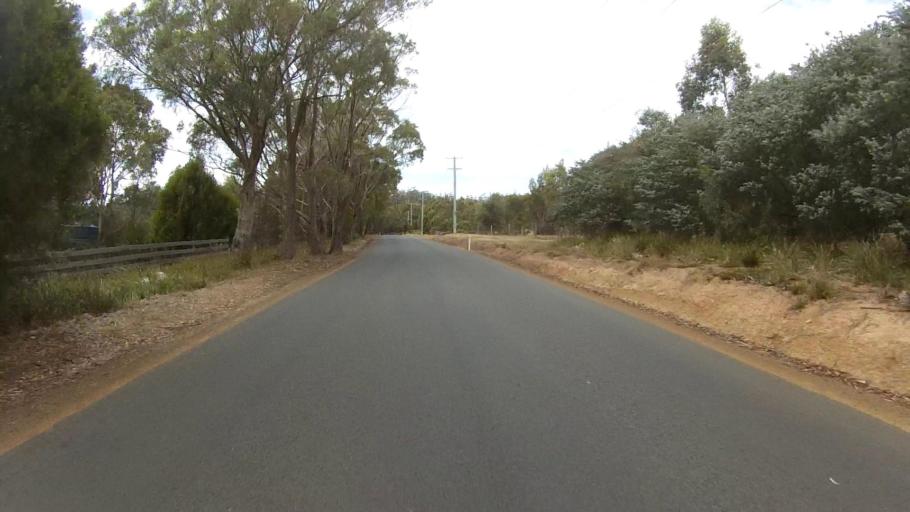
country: AU
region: Tasmania
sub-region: Kingborough
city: Blackmans Bay
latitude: -43.0236
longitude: 147.3045
